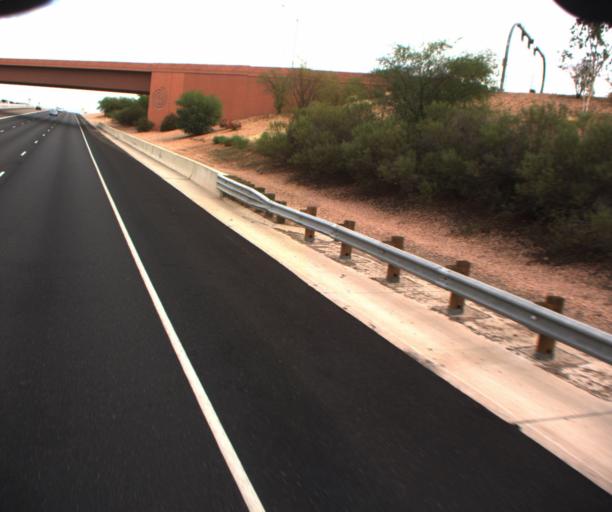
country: US
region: Arizona
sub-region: Maricopa County
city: Mesa
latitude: 33.4684
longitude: -111.7826
